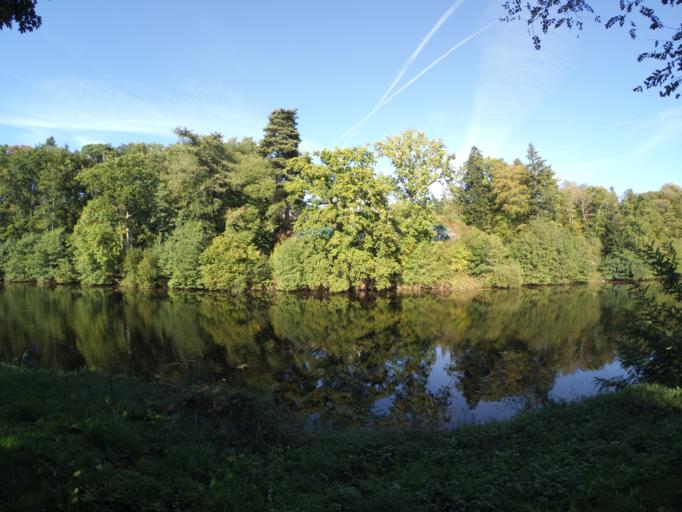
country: FR
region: Brittany
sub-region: Departement du Morbihan
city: Saint-Martin-sur-Oust
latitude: 47.7406
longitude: -2.2337
